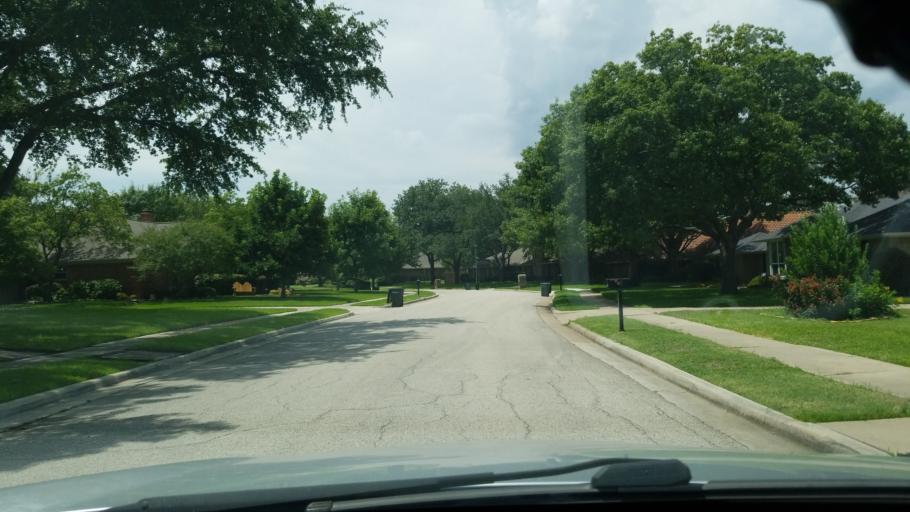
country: US
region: Texas
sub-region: Dallas County
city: Coppell
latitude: 32.9627
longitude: -96.9784
